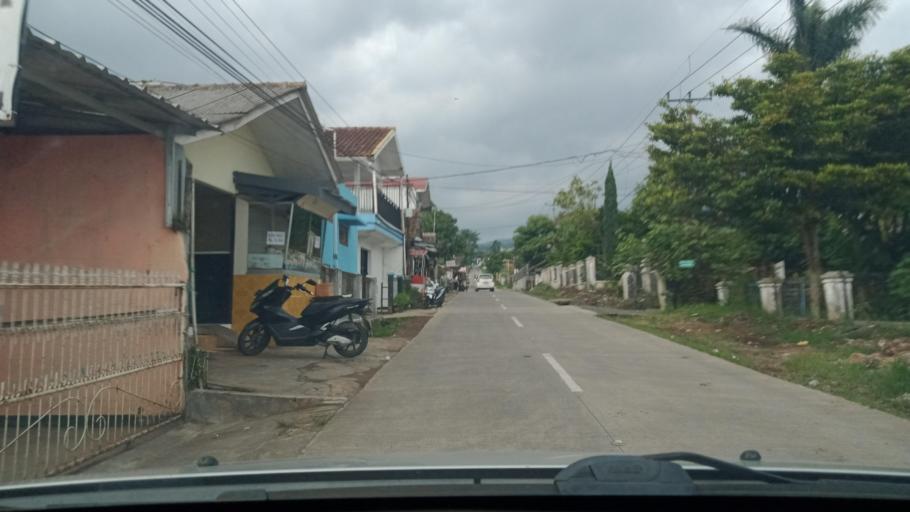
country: ID
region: West Java
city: Lembang
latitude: -6.8070
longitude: 107.5780
